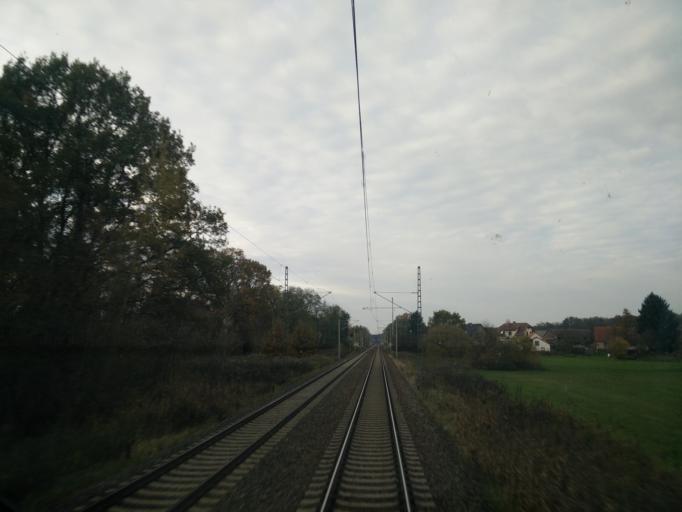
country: DE
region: Brandenburg
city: Halbe
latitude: 52.0875
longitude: 13.7215
